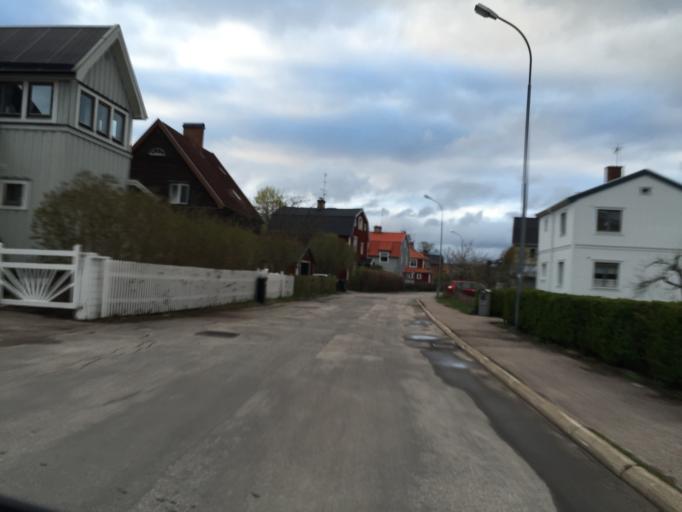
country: SE
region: Dalarna
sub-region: Ludvika Kommun
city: Ludvika
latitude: 60.1421
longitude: 15.1951
